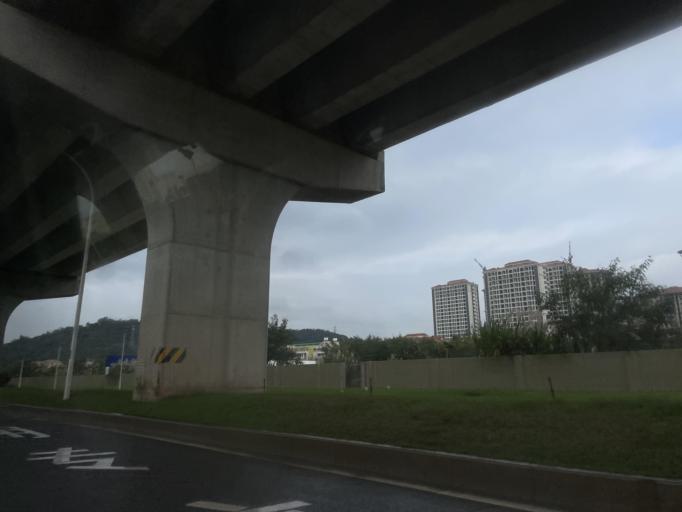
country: CN
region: Guangdong
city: Wanzai
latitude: 22.1765
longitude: 113.4891
